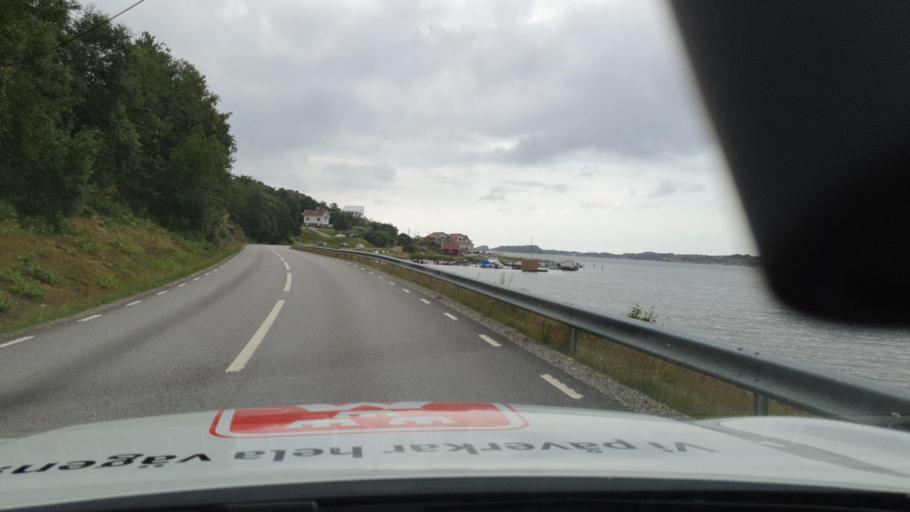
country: SE
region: Vaestra Goetaland
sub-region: Sotenas Kommun
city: Hunnebostrand
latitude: 58.4845
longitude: 11.3452
